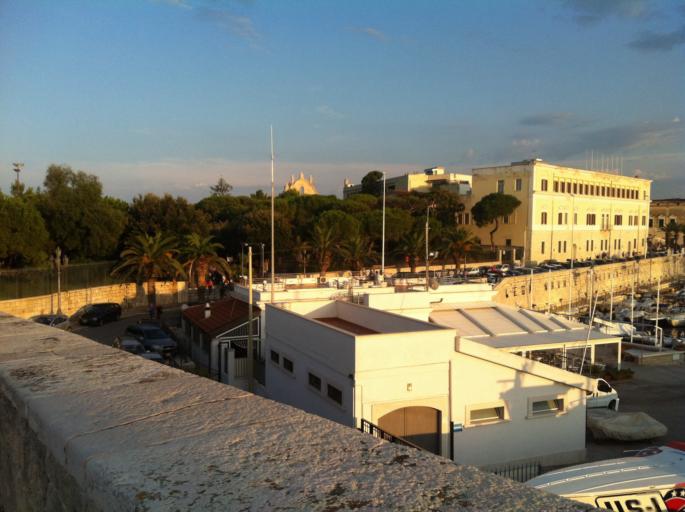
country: IT
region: Apulia
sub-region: Provincia di Barletta - Andria - Trani
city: Trani
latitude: 41.2805
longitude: 16.4225
